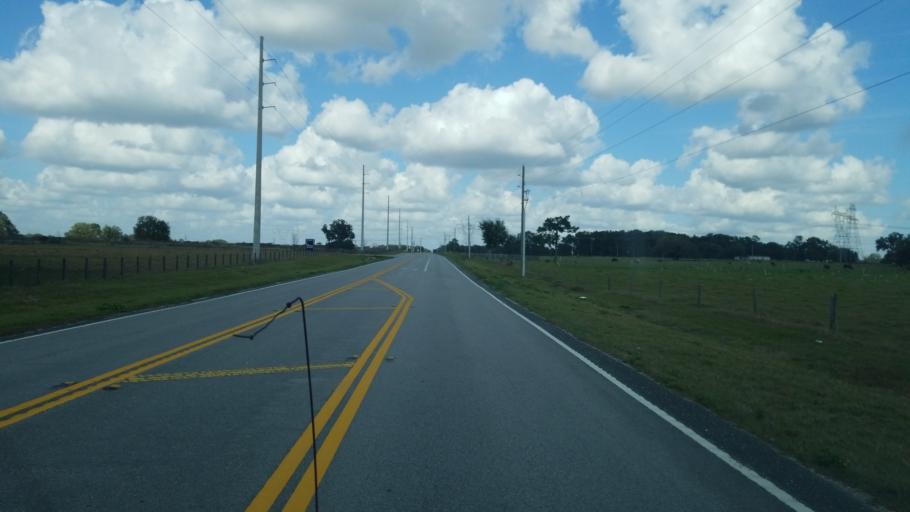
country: US
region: Florida
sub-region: Sumter County
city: Wildwood
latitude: 28.8891
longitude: -82.1200
